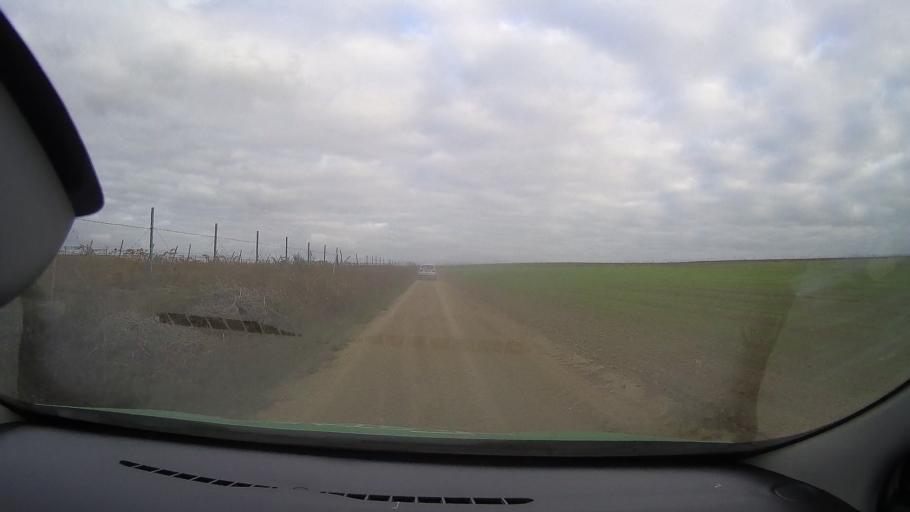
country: RO
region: Tulcea
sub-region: Comuna Jurilovca
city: Jurilovca
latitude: 44.7681
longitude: 28.9068
